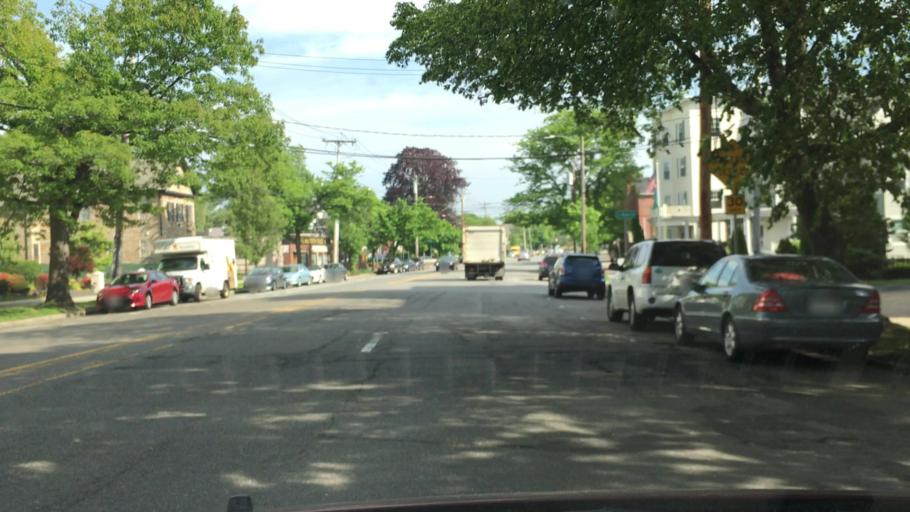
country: US
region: Massachusetts
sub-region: Middlesex County
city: Arlington
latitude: 42.4130
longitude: -71.1494
